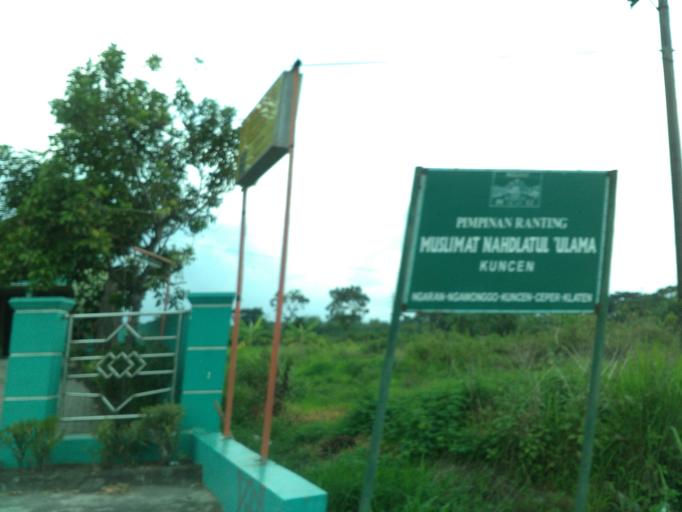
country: ID
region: Central Java
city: Ceper
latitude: -7.6554
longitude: 110.6796
